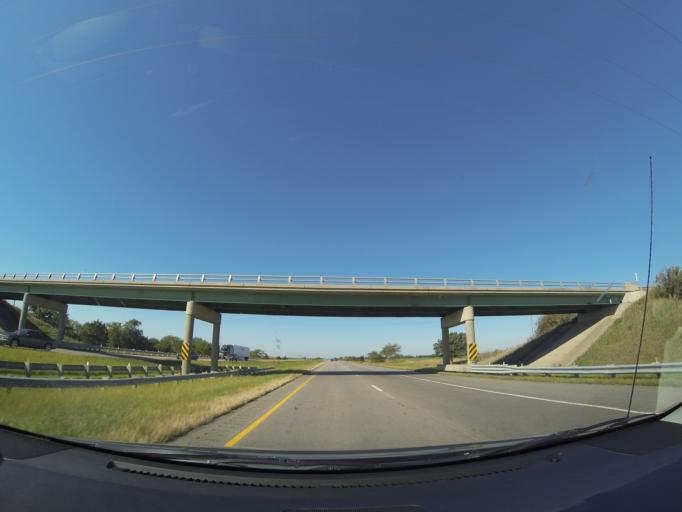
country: US
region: Nebraska
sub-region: Saline County
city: Friend
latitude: 40.8226
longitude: -97.2533
